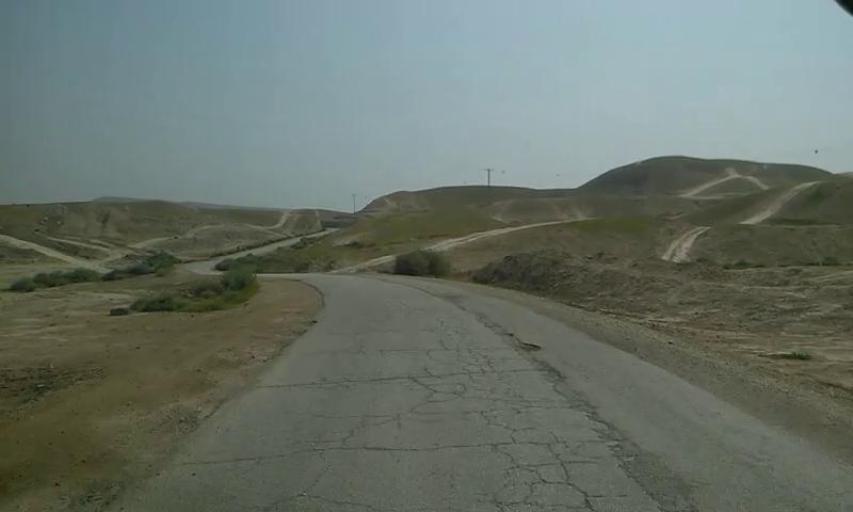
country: PS
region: West Bank
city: Jericho
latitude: 31.7957
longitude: 35.4268
